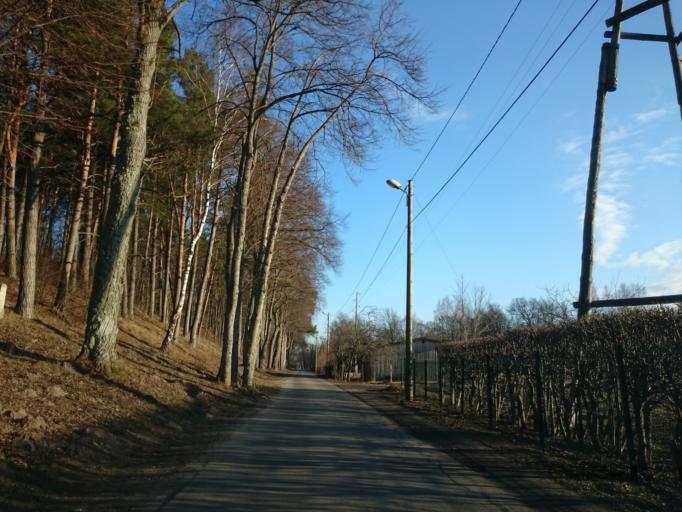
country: LV
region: Carnikava
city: Carnikava
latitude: 57.1250
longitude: 24.3208
